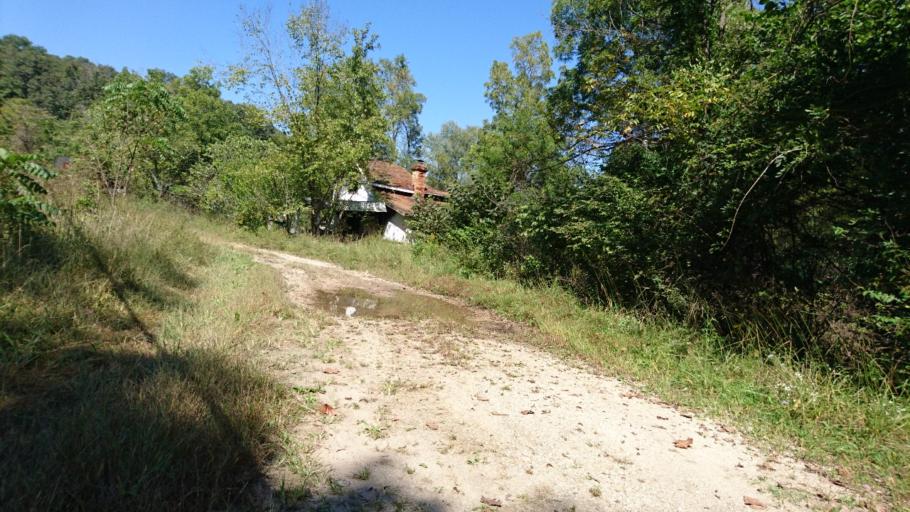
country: US
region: Missouri
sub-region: Phelps County
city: Rolla
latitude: 37.9371
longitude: -91.8422
